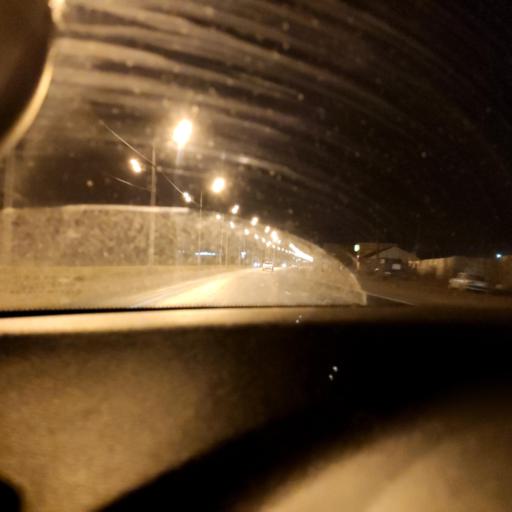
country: RU
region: Samara
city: Smyshlyayevka
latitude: 53.2584
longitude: 50.3756
